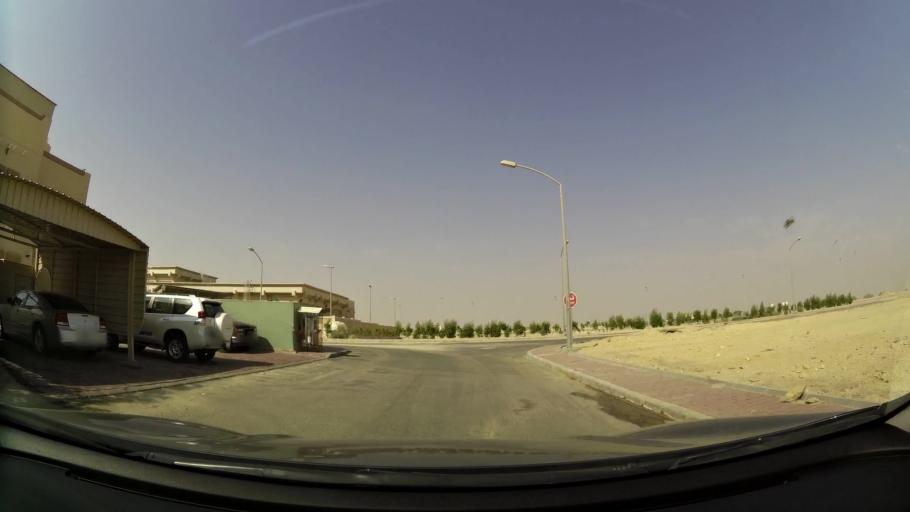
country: KW
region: Al Ahmadi
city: Al Wafrah
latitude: 28.8101
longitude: 48.0503
